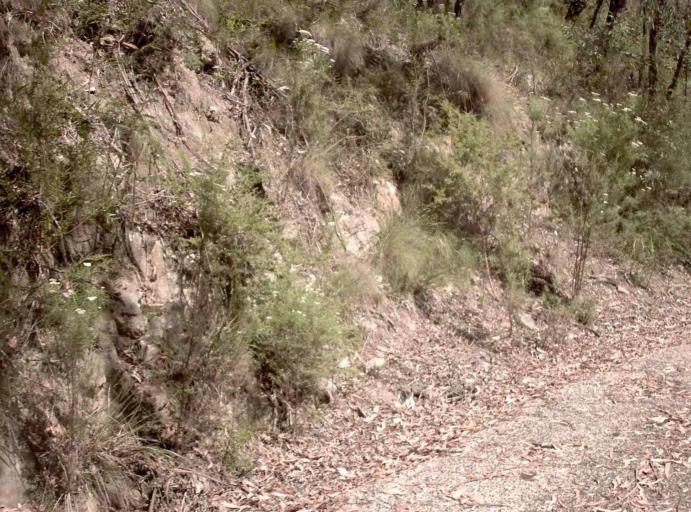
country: AU
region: Victoria
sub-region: East Gippsland
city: Lakes Entrance
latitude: -37.3666
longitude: 148.2182
